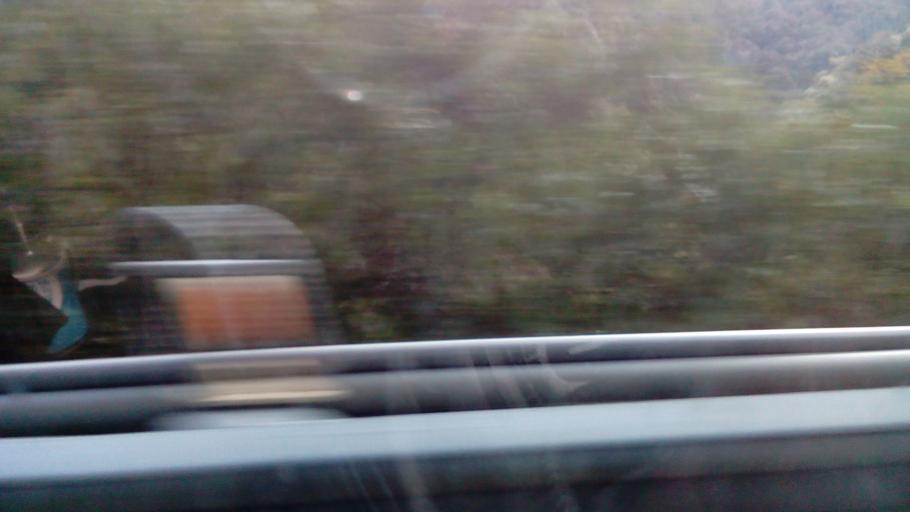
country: TW
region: Taiwan
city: Daxi
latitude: 24.4107
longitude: 121.3601
